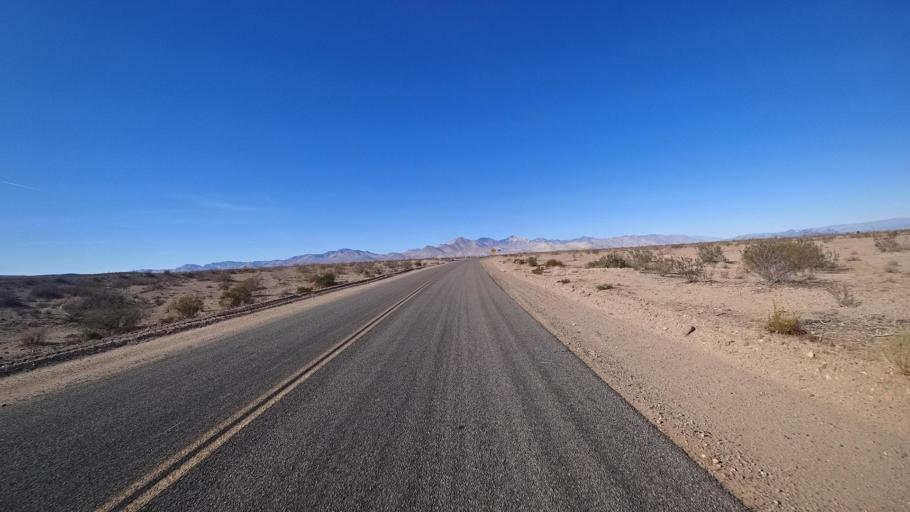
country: US
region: California
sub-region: Kern County
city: China Lake Acres
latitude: 35.5626
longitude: -117.7750
